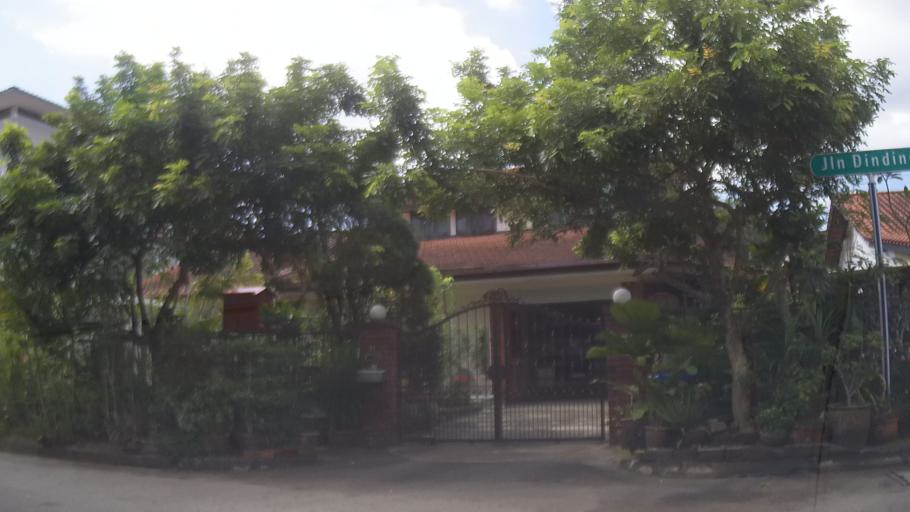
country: MY
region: Johor
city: Johor Bahru
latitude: 1.4158
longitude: 103.7575
